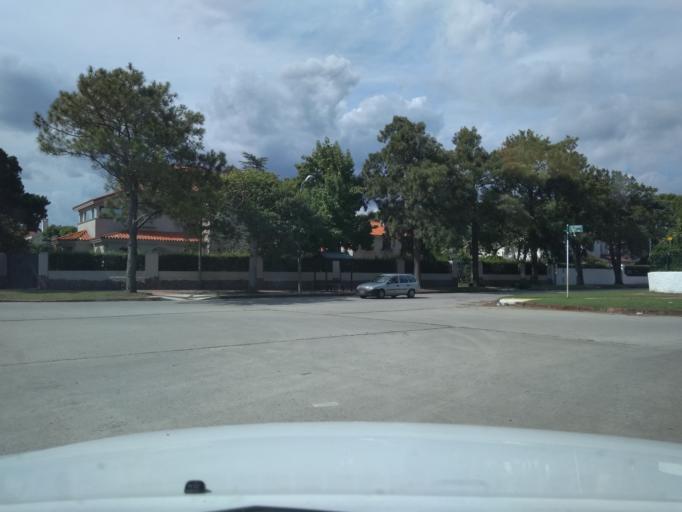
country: UY
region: Canelones
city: Barra de Carrasco
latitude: -34.8888
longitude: -56.0539
